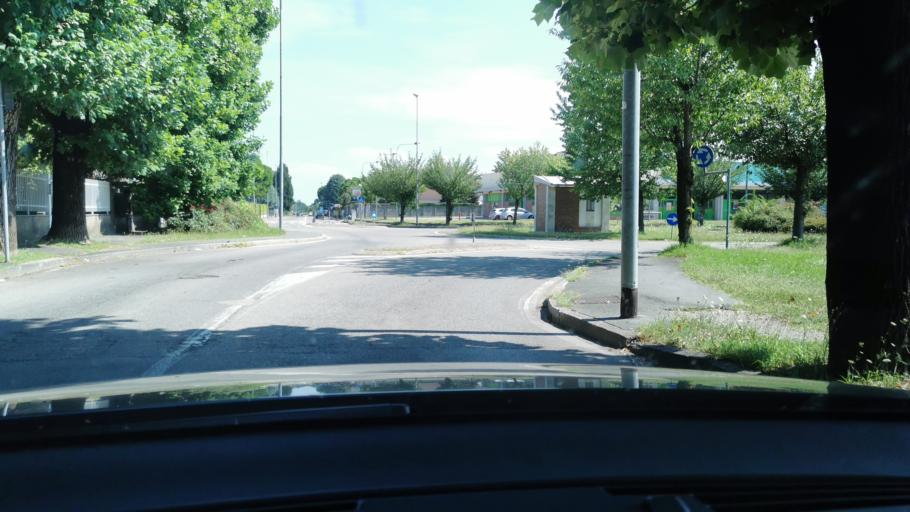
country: IT
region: Lombardy
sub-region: Citta metropolitana di Milano
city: Rescaldina
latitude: 45.6173
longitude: 8.9570
